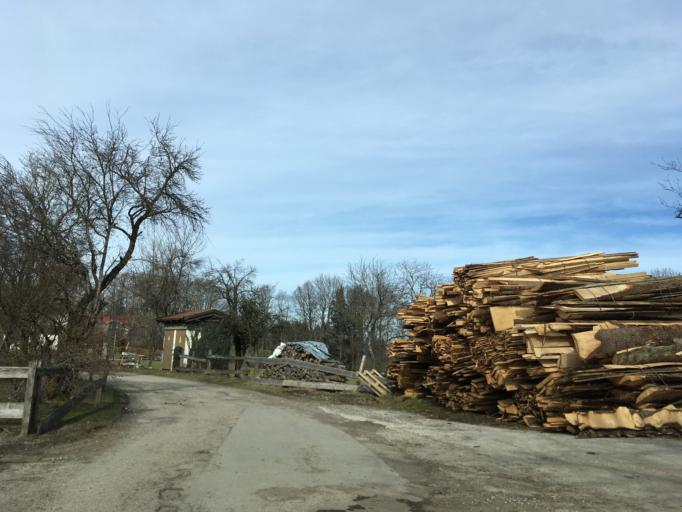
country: DE
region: Bavaria
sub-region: Upper Bavaria
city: Bernau am Chiemsee
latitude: 47.8174
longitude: 12.3444
